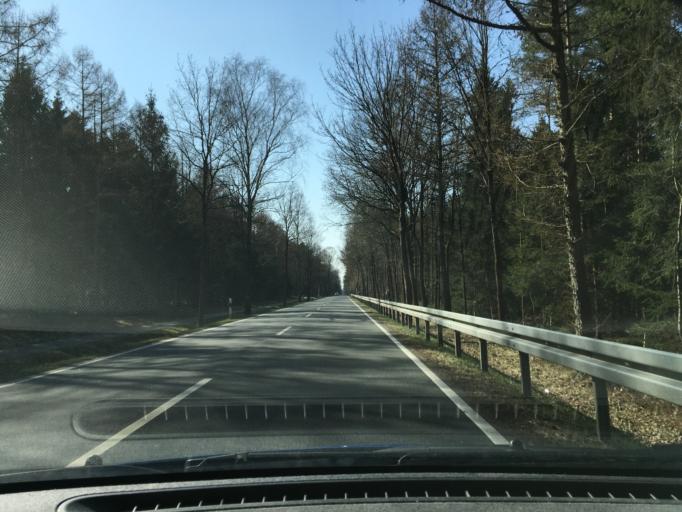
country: DE
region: Lower Saxony
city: Hermannsburg
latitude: 52.8218
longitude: 10.1638
